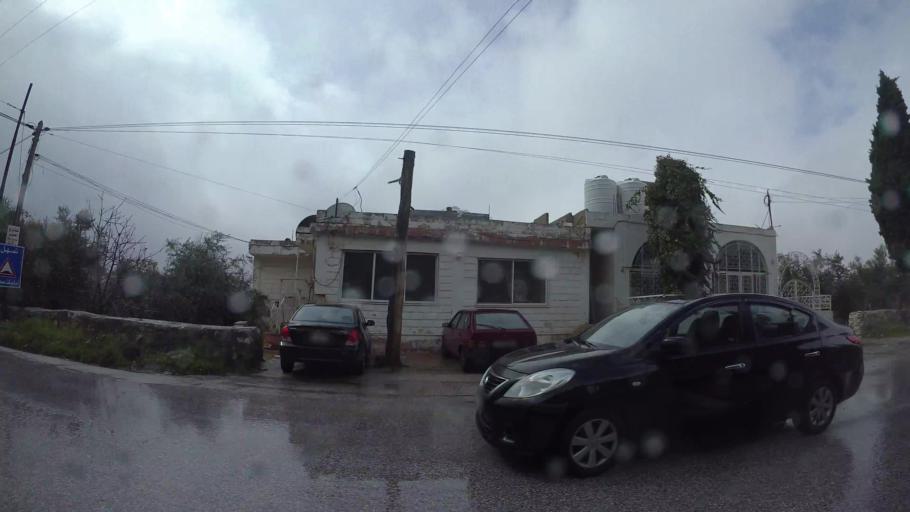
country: JO
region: Amman
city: Wadi as Sir
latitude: 32.0112
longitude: 35.7969
